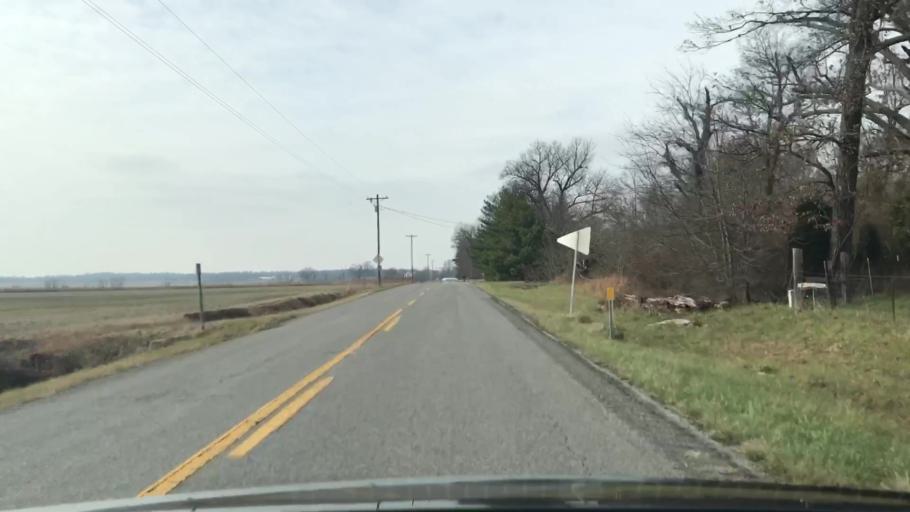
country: US
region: Kentucky
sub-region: McLean County
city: Calhoun
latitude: 37.5150
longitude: -87.4039
